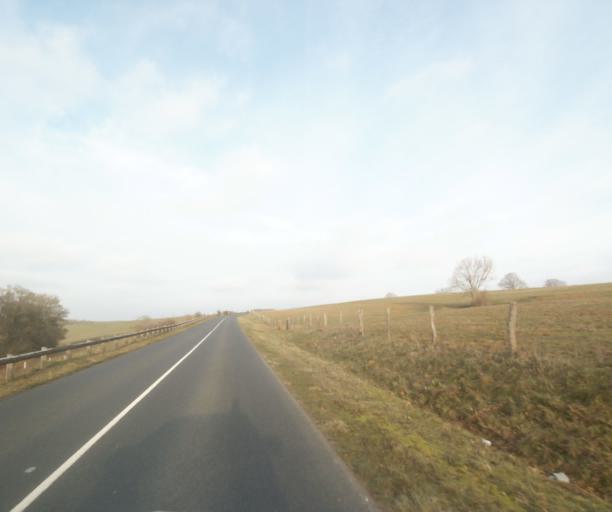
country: FR
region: Champagne-Ardenne
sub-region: Departement de la Marne
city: Sermaize-les-Bains
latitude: 48.7251
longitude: 4.9383
